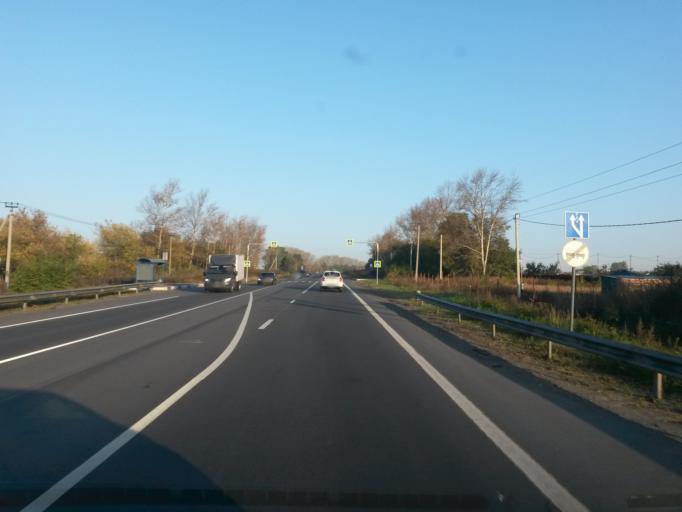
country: RU
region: Moskovskaya
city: Barybino
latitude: 55.2522
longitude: 37.8405
